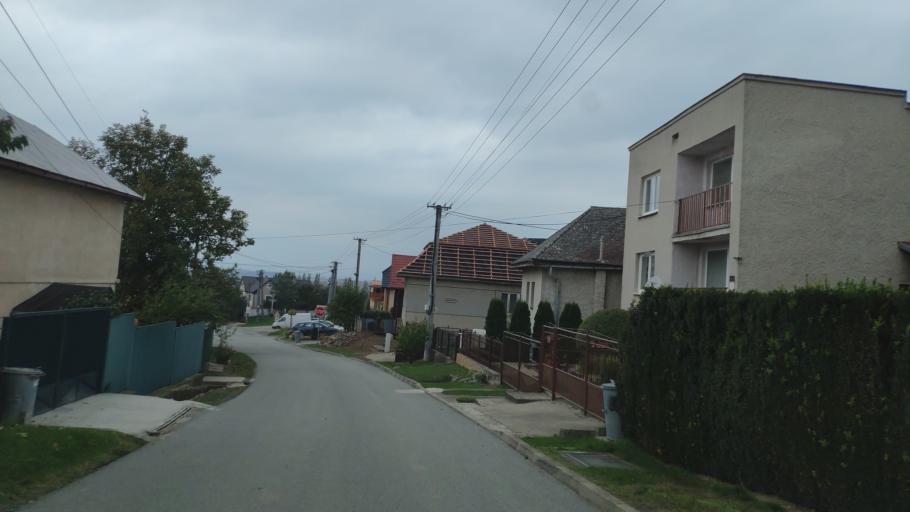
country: SK
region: Kosicky
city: Kosice
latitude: 48.6364
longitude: 21.3848
